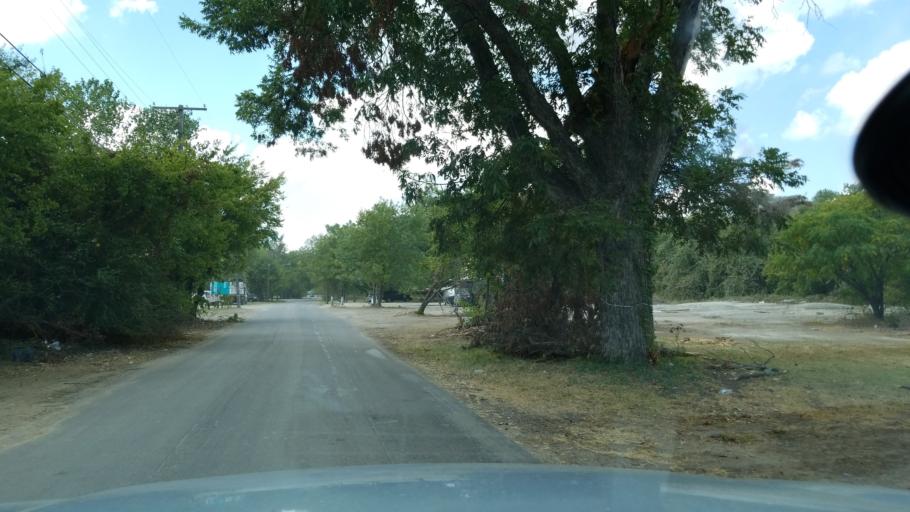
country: US
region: Texas
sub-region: Dallas County
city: Dallas
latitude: 32.7752
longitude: -96.8294
